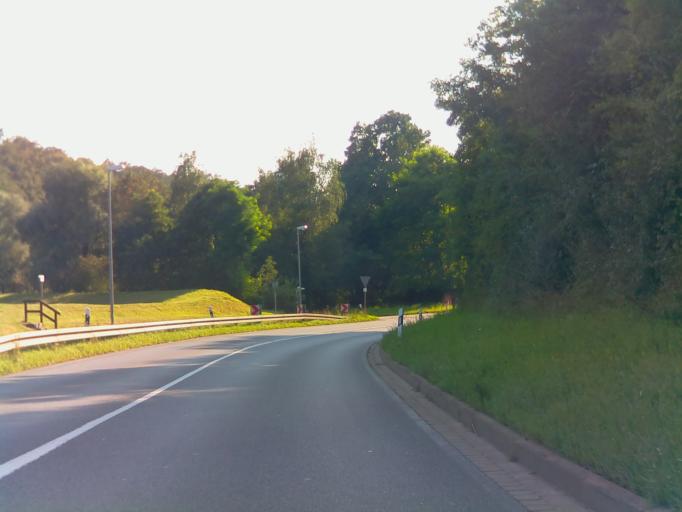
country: DE
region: Bavaria
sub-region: Regierungsbezirk Unterfranken
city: Sailauf
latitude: 50.0086
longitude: 9.2728
